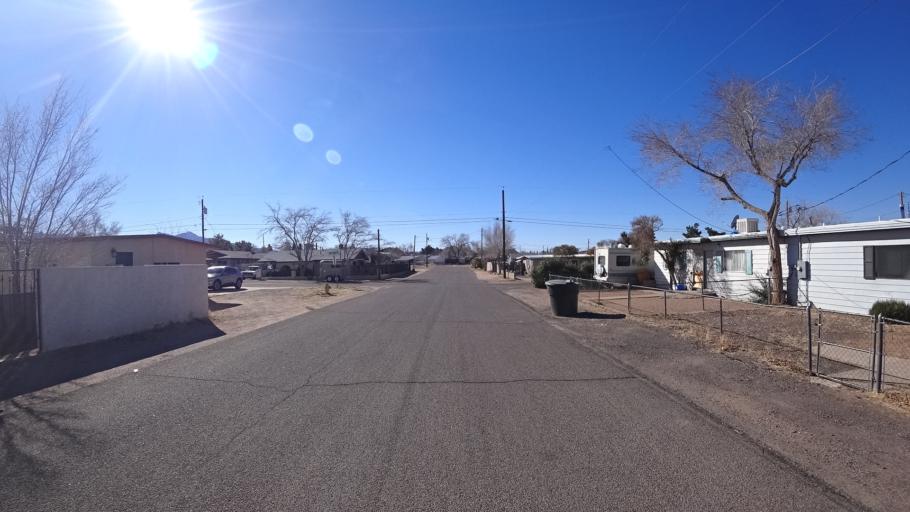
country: US
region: Arizona
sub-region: Mohave County
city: Kingman
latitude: 35.2042
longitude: -114.0270
